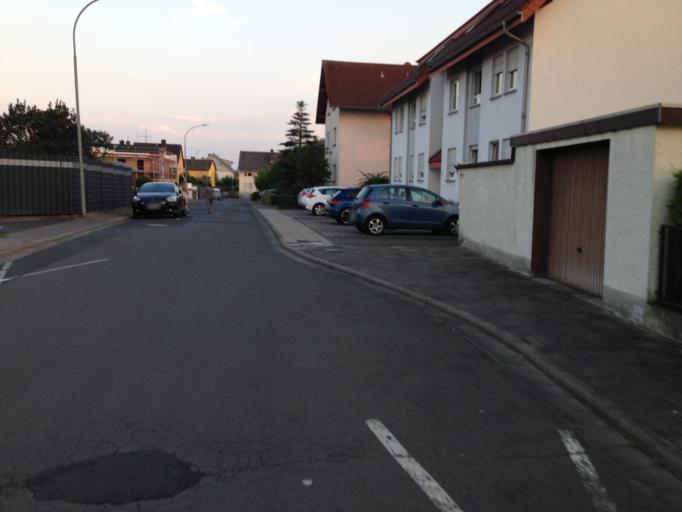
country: DE
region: Hesse
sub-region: Regierungsbezirk Giessen
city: Langgons
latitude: 50.5275
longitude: 8.6587
